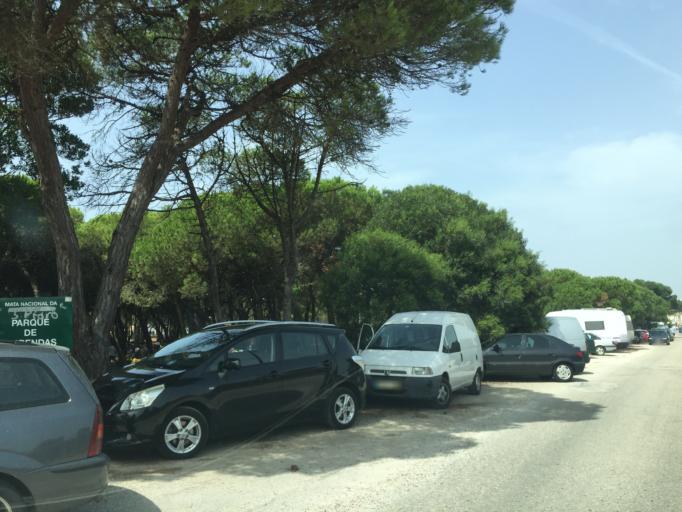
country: PT
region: Coimbra
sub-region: Figueira da Foz
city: Figueira da Foz
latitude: 40.1235
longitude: -8.8574
